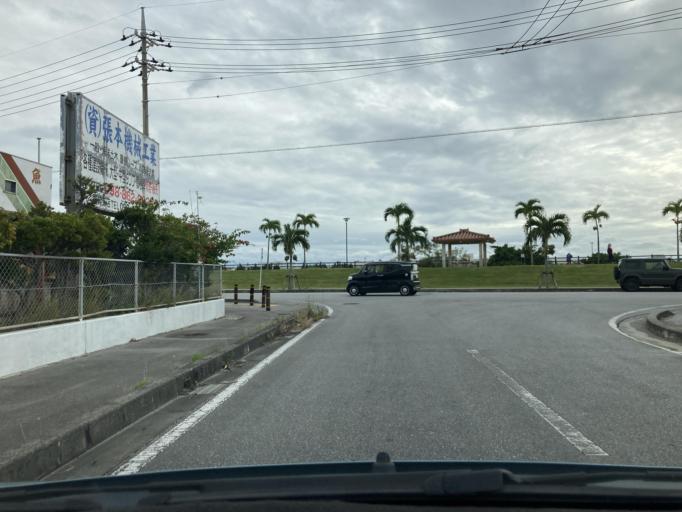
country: JP
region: Okinawa
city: Itoman
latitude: 26.1526
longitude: 127.6571
